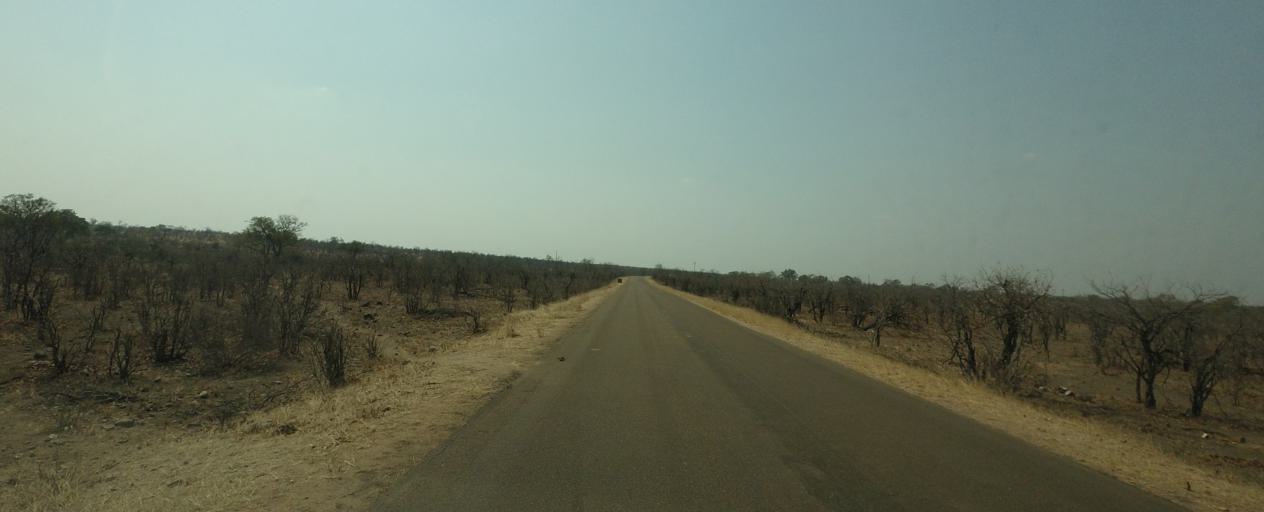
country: ZA
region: Limpopo
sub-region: Mopani District Municipality
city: Giyani
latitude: -23.2417
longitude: 31.3151
